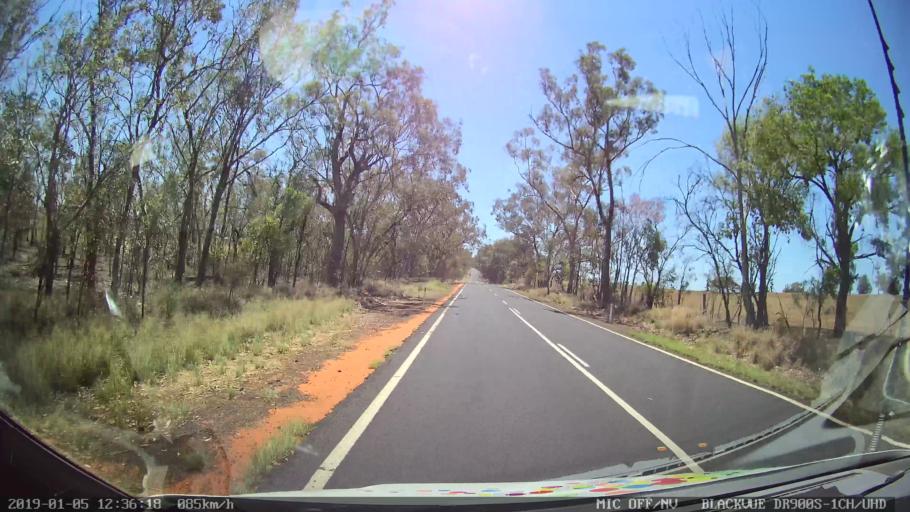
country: AU
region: New South Wales
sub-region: Warrumbungle Shire
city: Coonabarabran
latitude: -31.2075
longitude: 149.4382
